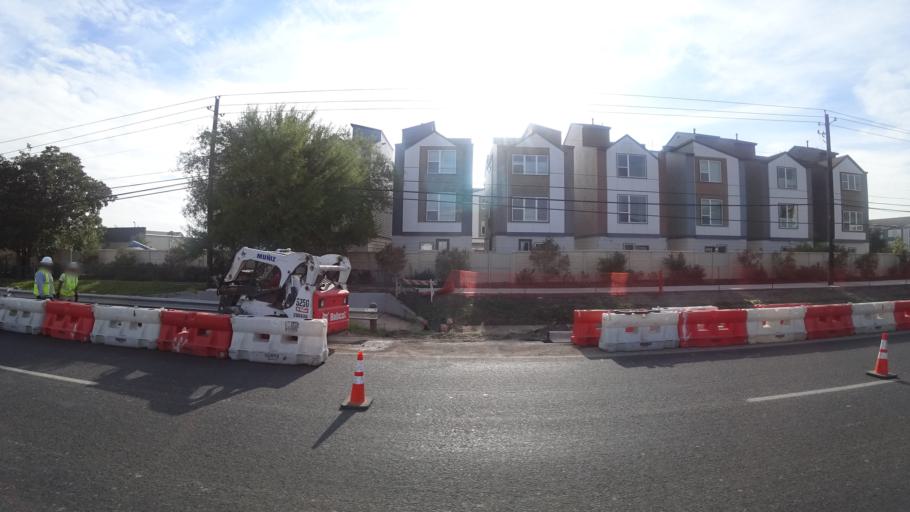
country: US
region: Texas
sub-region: Travis County
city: Austin
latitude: 30.2393
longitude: -97.7192
